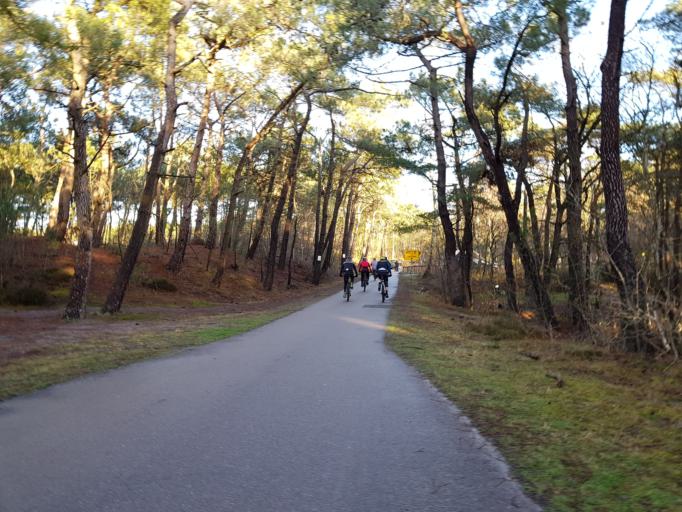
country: NL
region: North Holland
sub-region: Gemeente Bergen
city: Egmond aan Zee
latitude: 52.6976
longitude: 4.6689
